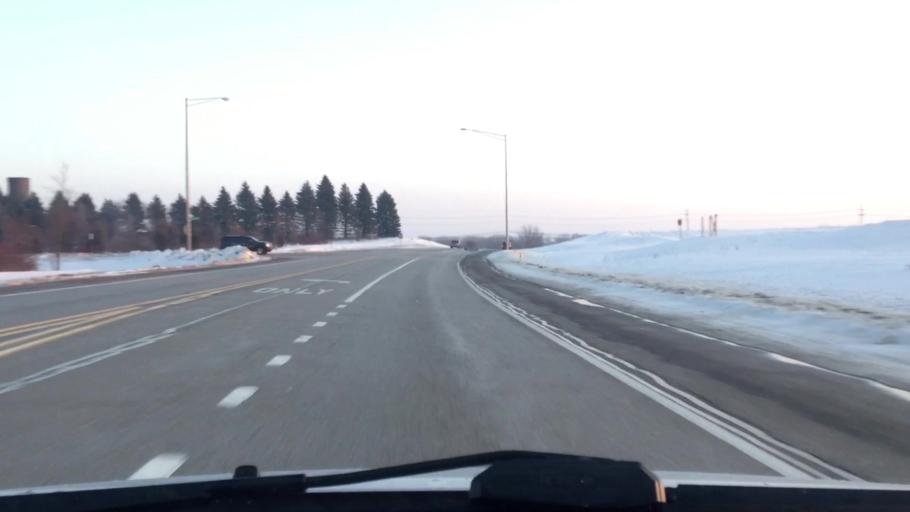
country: US
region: Illinois
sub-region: Kane County
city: Village of Campton Hills
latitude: 41.9422
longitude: -88.3982
